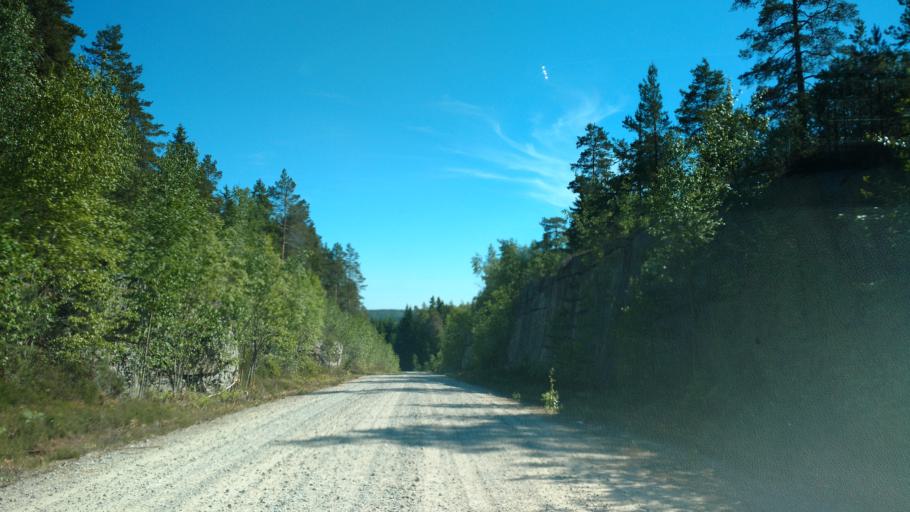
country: FI
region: Varsinais-Suomi
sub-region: Salo
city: Halikko
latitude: 60.4306
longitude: 22.9564
